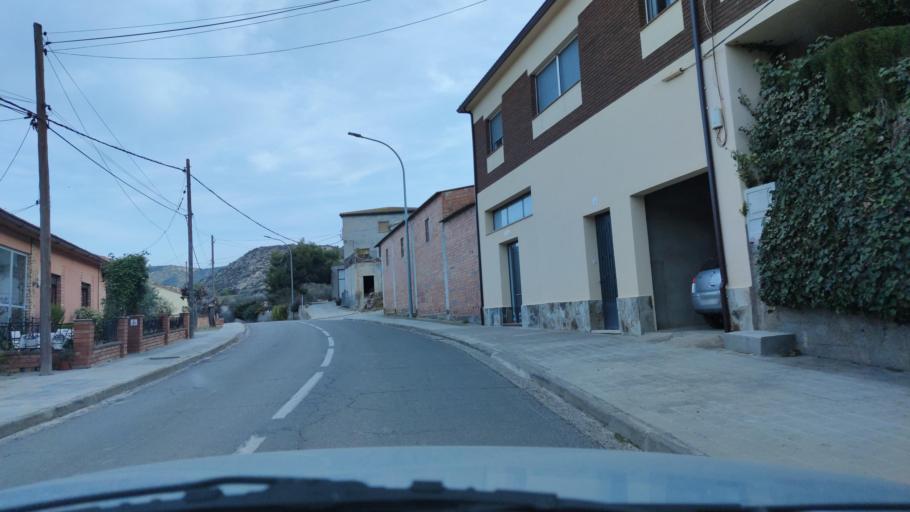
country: ES
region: Catalonia
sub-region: Provincia de Lleida
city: Balaguer
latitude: 41.8255
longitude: 0.8013
